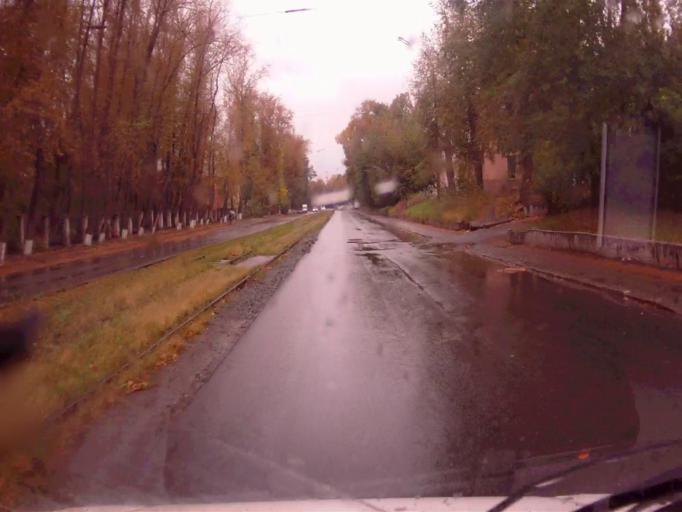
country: RU
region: Chelyabinsk
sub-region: Gorod Chelyabinsk
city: Chelyabinsk
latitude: 55.1886
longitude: 61.4131
